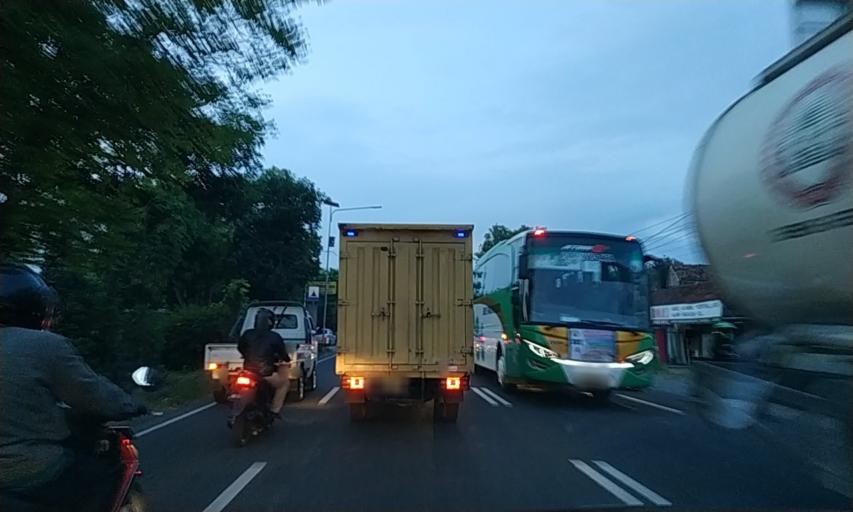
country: ID
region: Daerah Istimewa Yogyakarta
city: Srandakan
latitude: -7.8441
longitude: 110.2183
